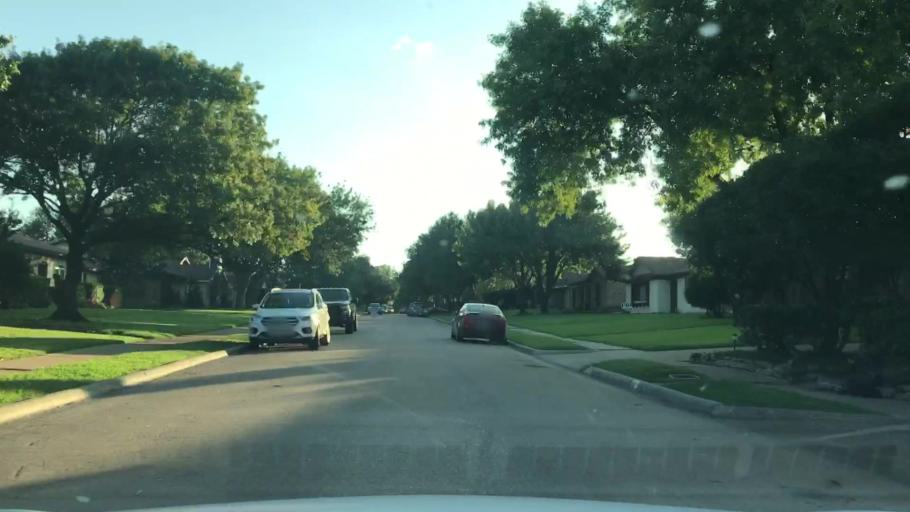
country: US
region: Texas
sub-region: Dallas County
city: Mesquite
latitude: 32.8106
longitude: -96.6472
